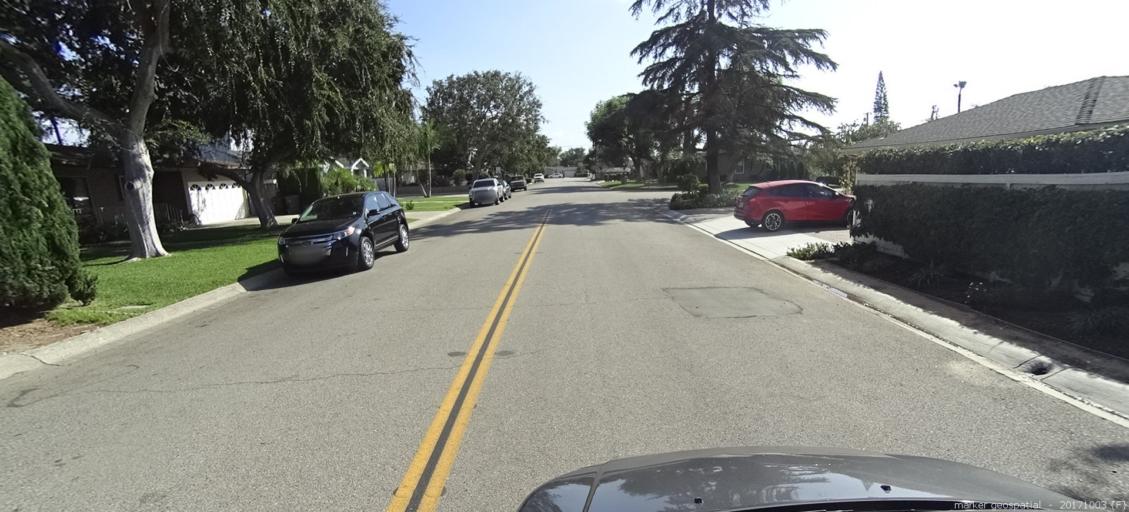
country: US
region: California
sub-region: Orange County
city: Garden Grove
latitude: 33.7768
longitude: -117.9684
